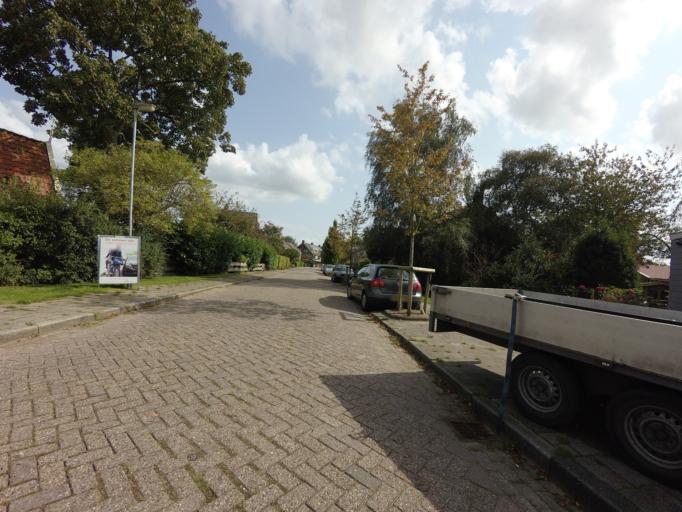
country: NL
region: North Holland
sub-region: Gemeente Waterland
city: Broek in Waterland
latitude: 52.4364
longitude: 4.9952
